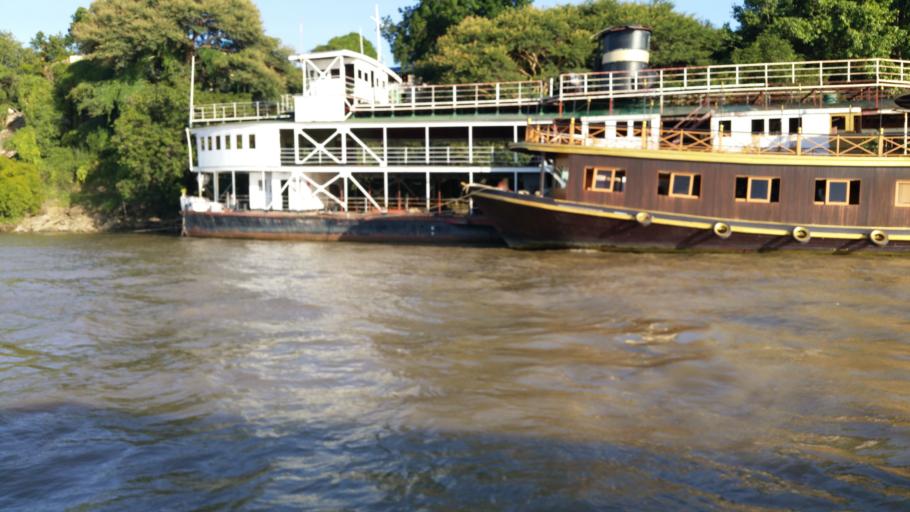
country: MM
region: Magway
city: Pakokku
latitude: 21.1825
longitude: 94.8637
